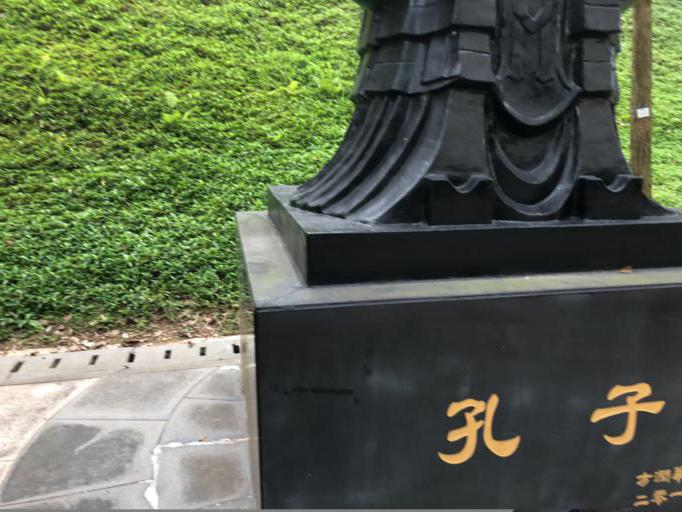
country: HK
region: Tai Po
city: Tai Po
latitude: 22.4691
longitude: 114.1940
